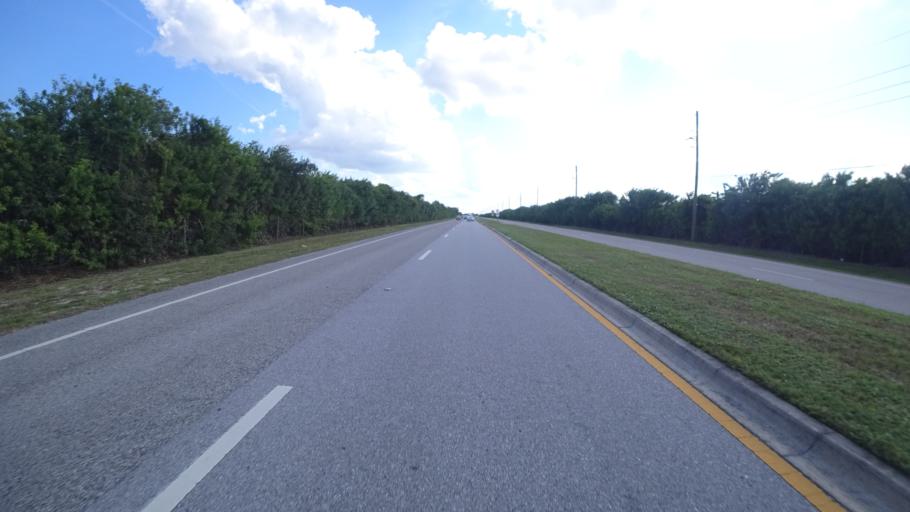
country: US
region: Florida
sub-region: Manatee County
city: Longboat Key
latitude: 27.4563
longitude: -82.6368
